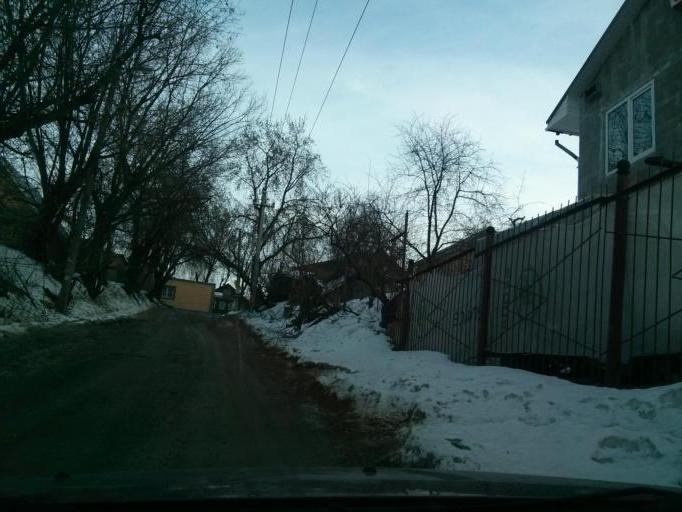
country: RU
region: Nizjnij Novgorod
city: Afonino
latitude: 56.2762
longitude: 44.0359
